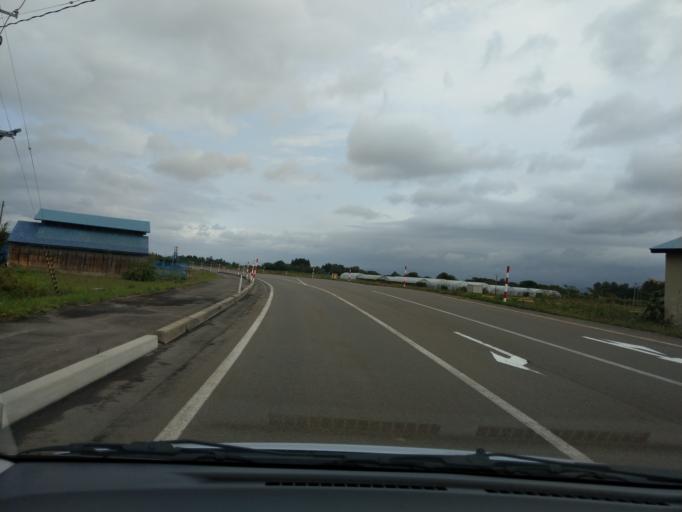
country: JP
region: Akita
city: Omagari
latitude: 39.3817
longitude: 140.4866
